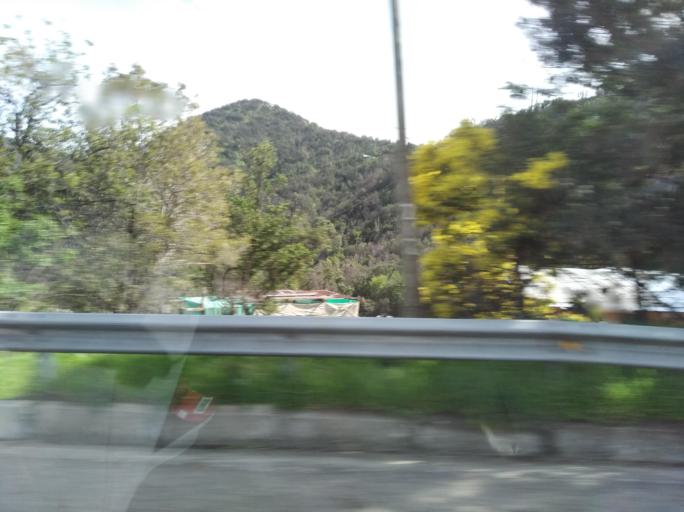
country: CL
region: Valparaiso
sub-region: Provincia de Marga Marga
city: Limache
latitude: -33.0593
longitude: -71.0524
